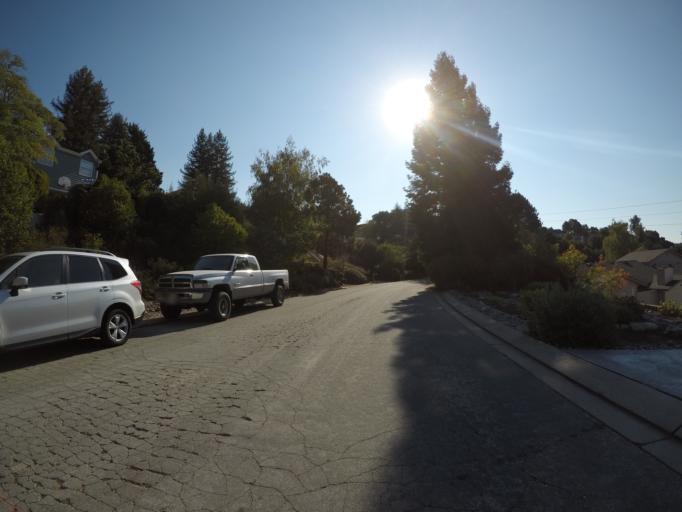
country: US
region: California
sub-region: Santa Cruz County
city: Scotts Valley
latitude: 37.0419
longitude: -122.0222
